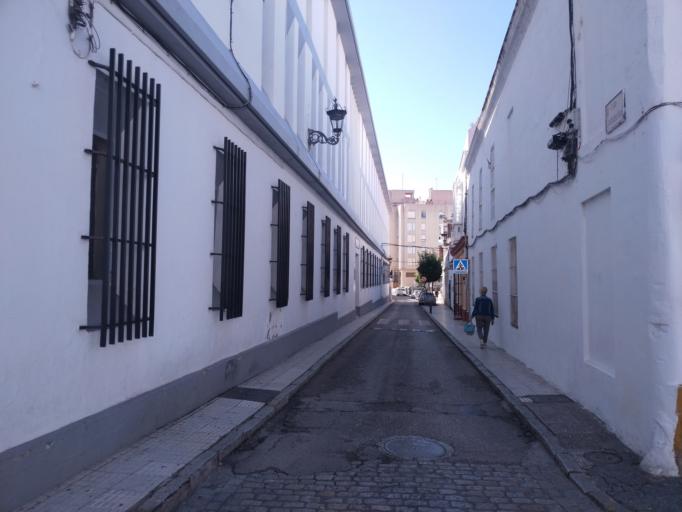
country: ES
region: Andalusia
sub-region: Provincia de Cadiz
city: San Fernando
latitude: 36.4688
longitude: -6.1971
